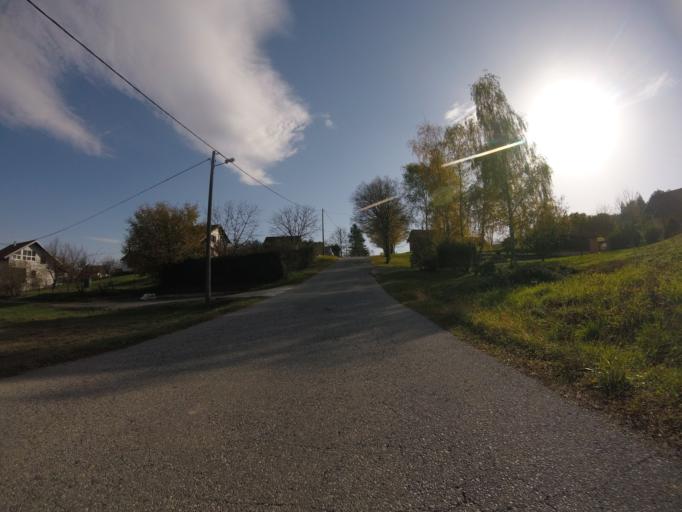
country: HR
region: Zagrebacka
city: Mraclin
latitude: 45.6157
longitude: 16.0728
